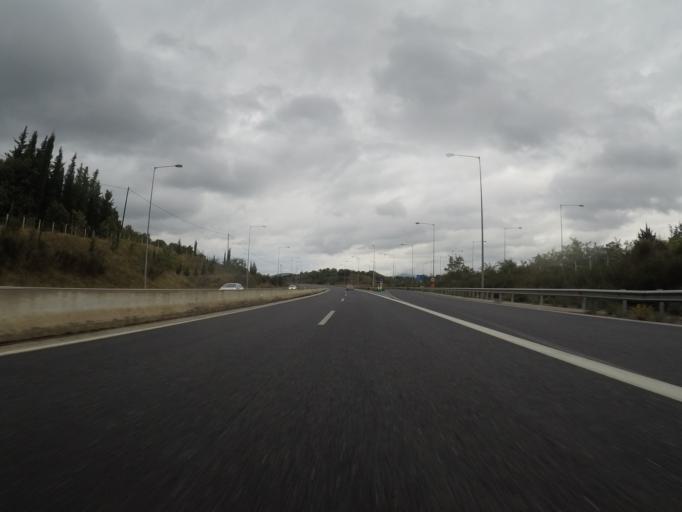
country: GR
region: Peloponnese
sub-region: Nomos Arkadias
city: Megalopoli
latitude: 37.3588
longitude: 22.1343
